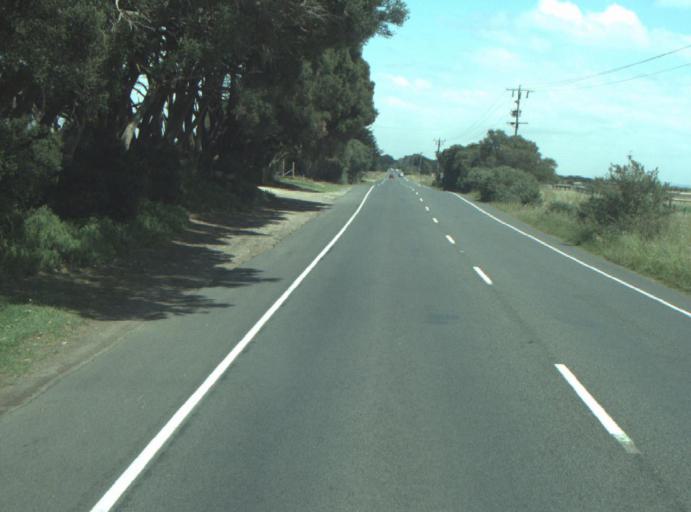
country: AU
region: Victoria
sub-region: Greater Geelong
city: Leopold
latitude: -38.2723
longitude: 144.4813
